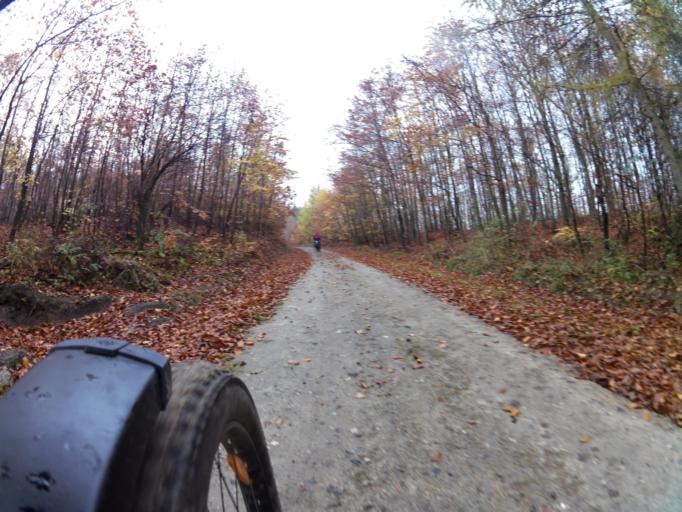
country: PL
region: Pomeranian Voivodeship
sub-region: Powiat pucki
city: Krokowa
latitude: 54.7760
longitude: 18.0913
